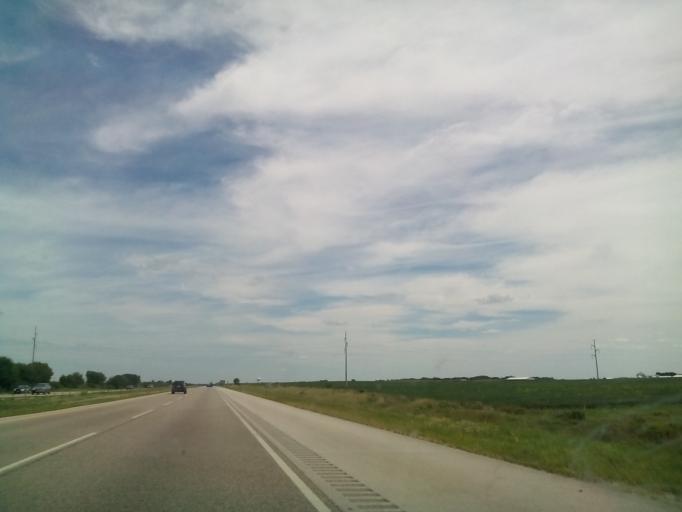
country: US
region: Illinois
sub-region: DeKalb County
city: Malta
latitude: 41.9000
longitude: -88.8145
